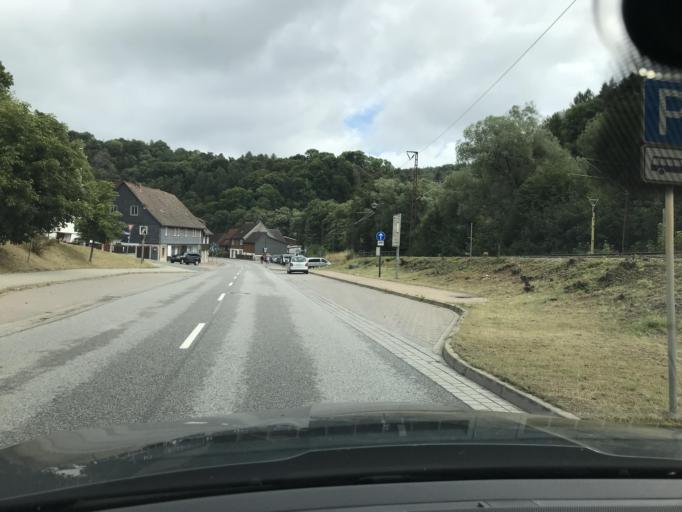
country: DE
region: Saxony-Anhalt
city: Rubeland
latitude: 51.7558
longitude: 10.8394
